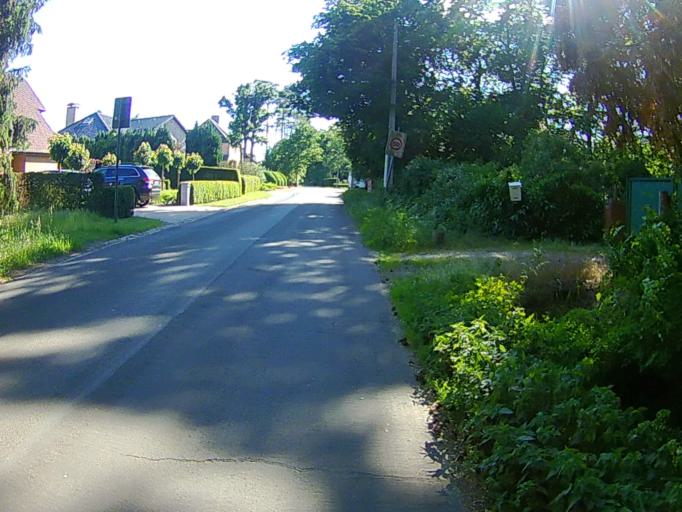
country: BE
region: Flanders
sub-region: Provincie Antwerpen
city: Herentals
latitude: 51.2018
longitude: 4.8323
